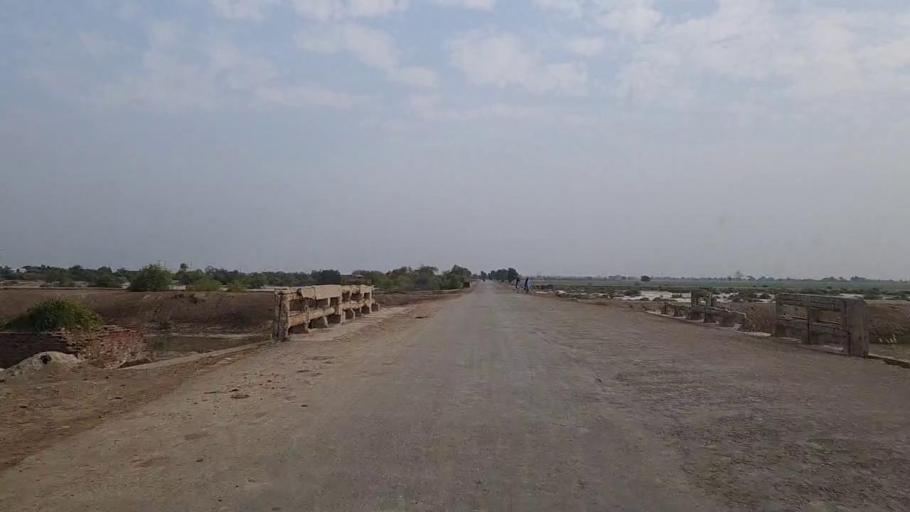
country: PK
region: Sindh
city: Mirwah Gorchani
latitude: 25.3769
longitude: 69.0967
